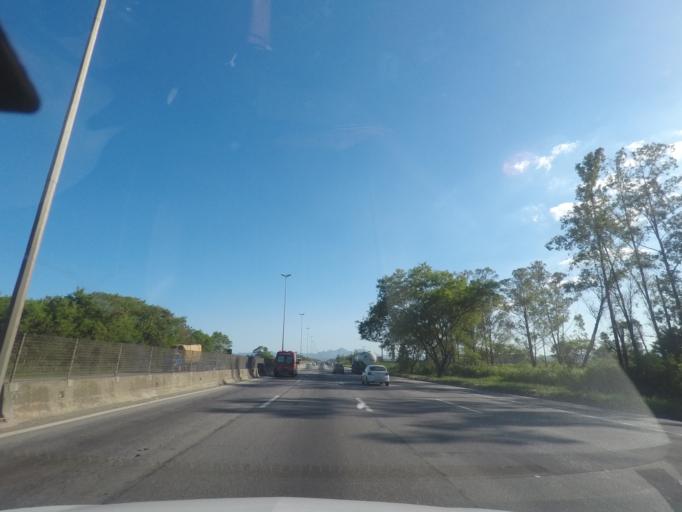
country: BR
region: Rio de Janeiro
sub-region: Duque De Caxias
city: Duque de Caxias
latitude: -22.7268
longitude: -43.2892
